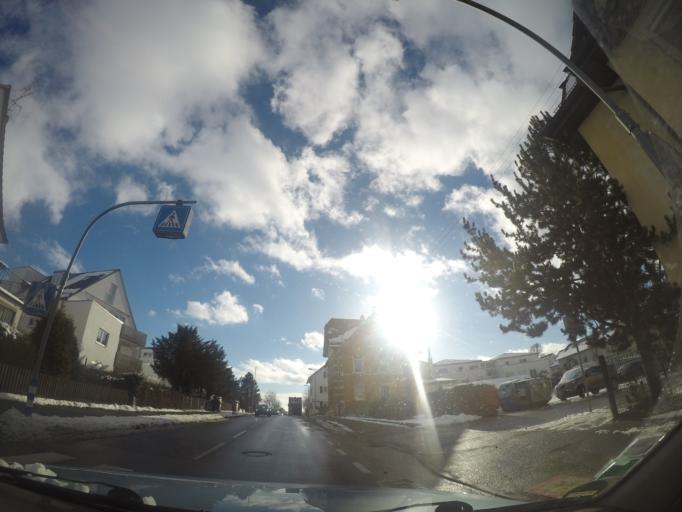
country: DE
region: Baden-Wuerttemberg
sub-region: Tuebingen Region
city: Ehingen
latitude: 48.2791
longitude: 9.7238
